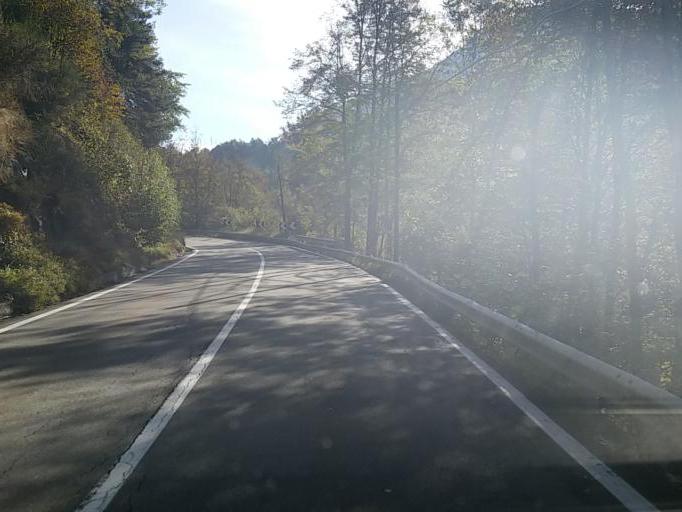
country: IT
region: Piedmont
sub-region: Provincia Verbano-Cusio-Ossola
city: Druogno
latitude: 46.1311
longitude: 8.4068
